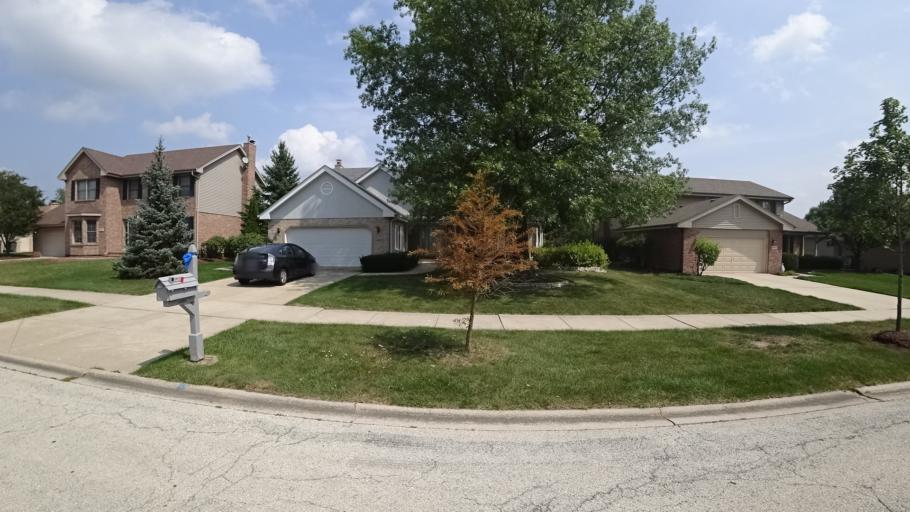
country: US
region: Illinois
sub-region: Will County
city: Goodings Grove
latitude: 41.6349
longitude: -87.9004
